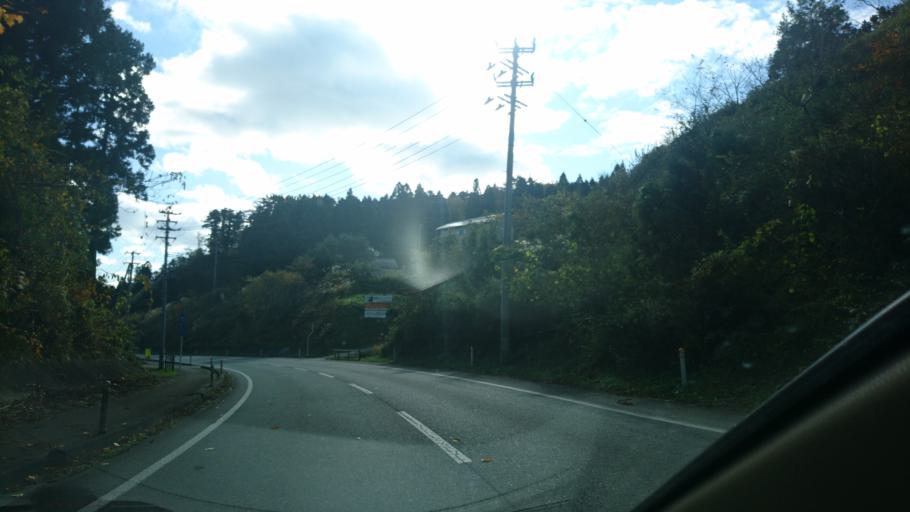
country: JP
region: Iwate
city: Ofunato
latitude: 39.0250
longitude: 141.7053
